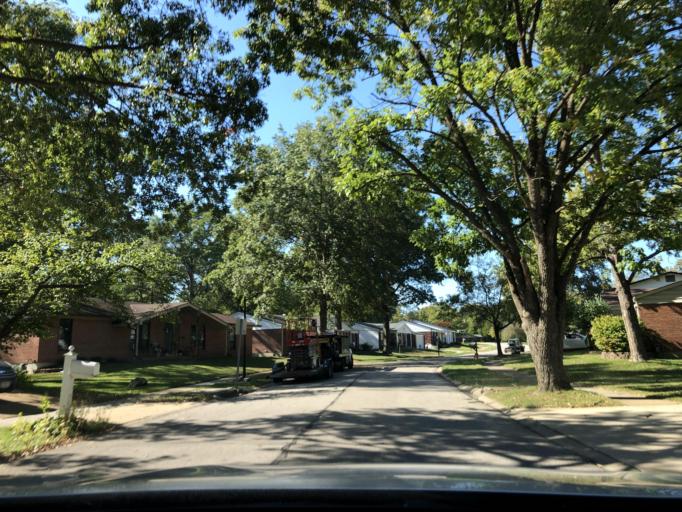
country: US
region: Missouri
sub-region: Saint Louis County
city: Concord
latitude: 38.4940
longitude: -90.3589
